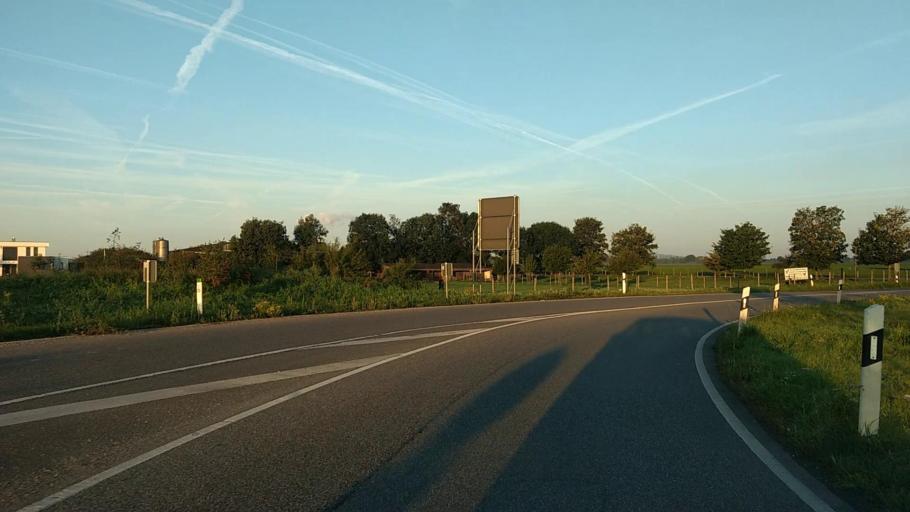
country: DE
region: North Rhine-Westphalia
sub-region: Regierungsbezirk Koln
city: Bergheim
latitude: 50.9318
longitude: 6.6413
